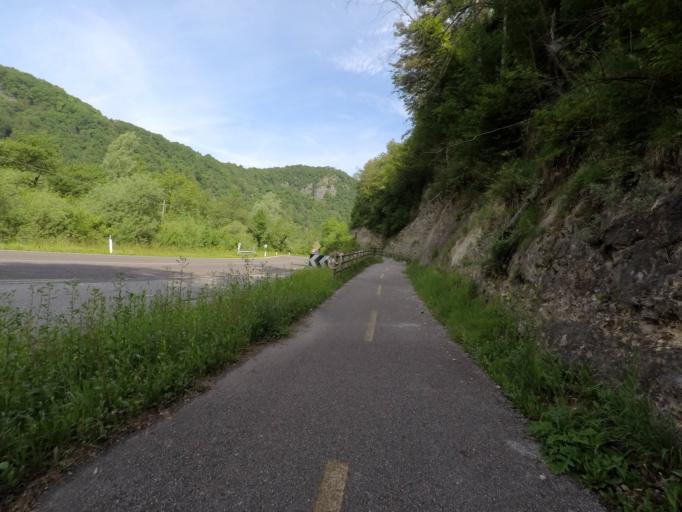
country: IT
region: Friuli Venezia Giulia
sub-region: Provincia di Udine
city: Cavazzo Carnico
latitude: 46.3698
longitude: 13.0327
